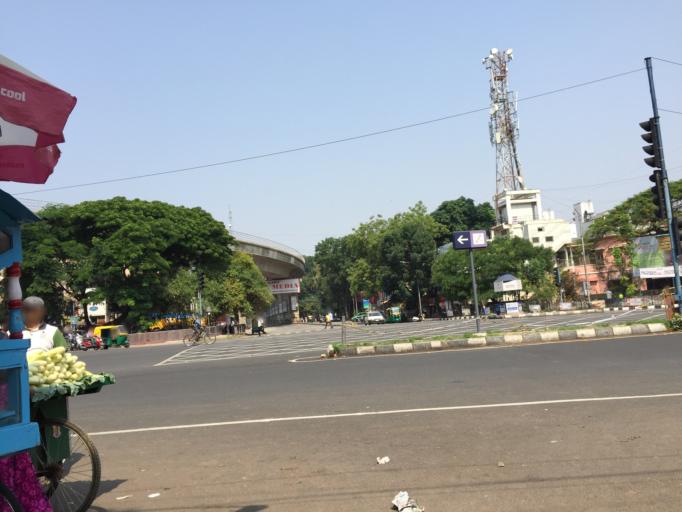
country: IN
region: Karnataka
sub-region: Bangalore Urban
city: Bangalore
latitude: 12.9483
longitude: 77.5803
